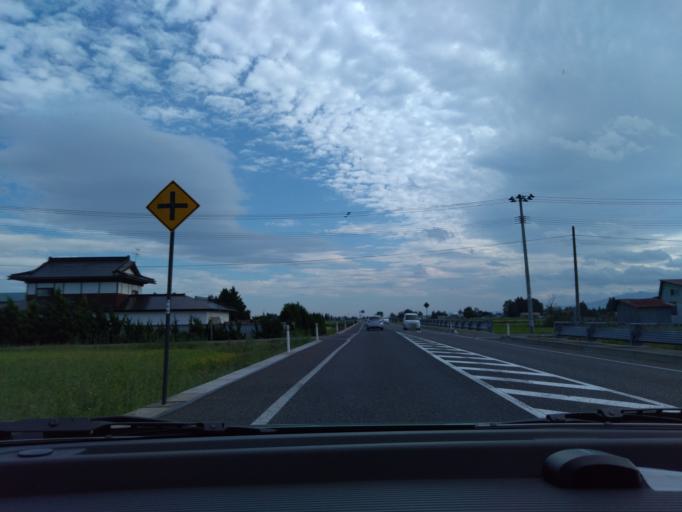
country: JP
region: Iwate
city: Hanamaki
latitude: 39.3729
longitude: 141.0572
